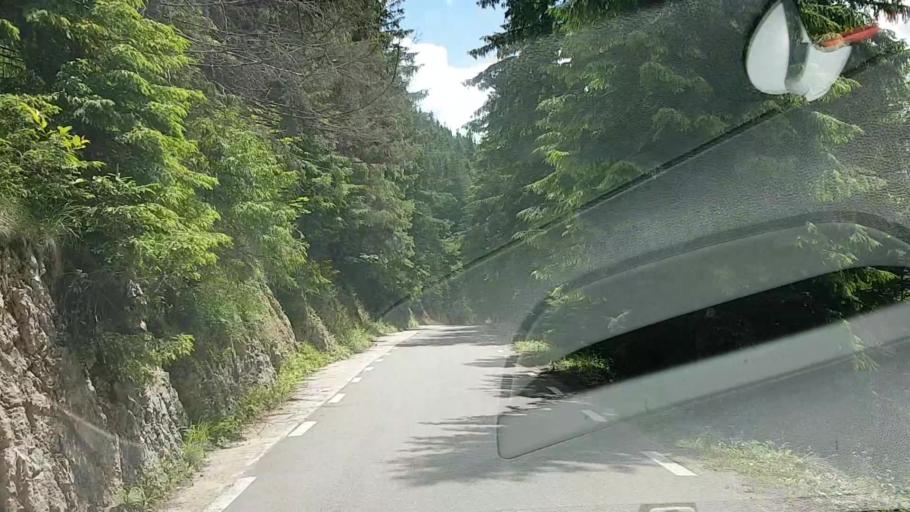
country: RO
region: Suceava
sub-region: Municipiul Campulung Moldovenesc
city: Campulung Moldovenesc
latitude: 47.4490
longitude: 25.5523
